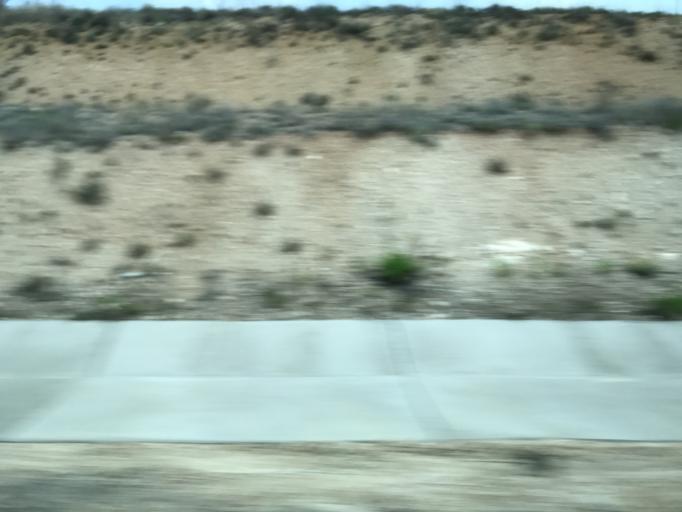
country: ES
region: Castille and Leon
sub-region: Provincia de Burgos
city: Villanueva de Gumiel
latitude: 41.7367
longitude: -3.6883
